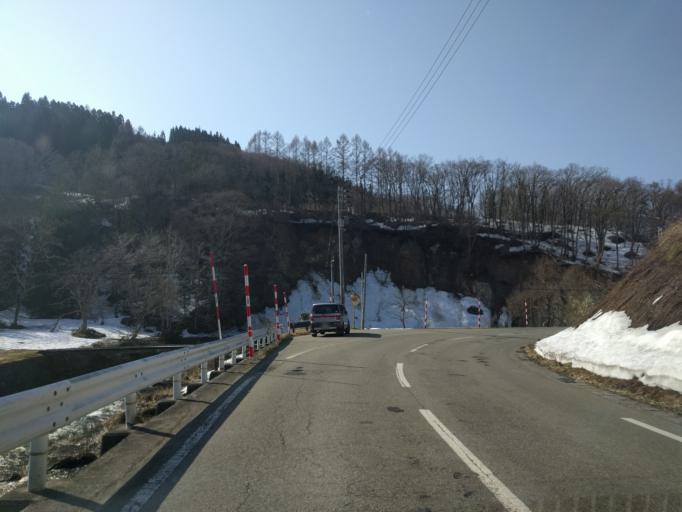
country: JP
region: Niigata
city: Muramatsu
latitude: 37.3377
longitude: 139.4715
